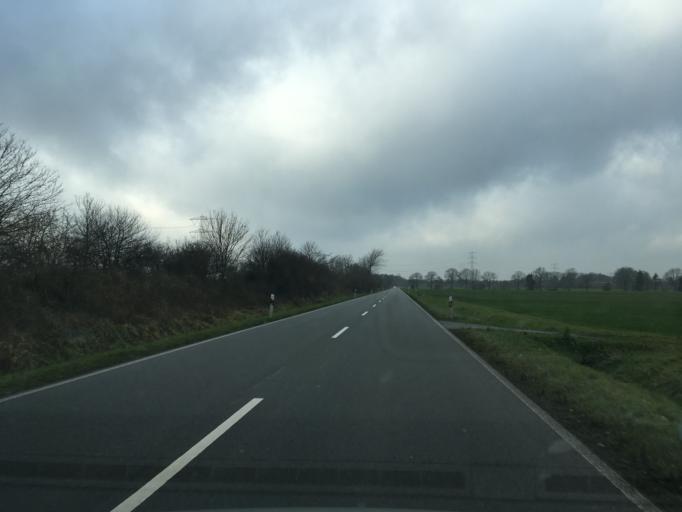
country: DE
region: North Rhine-Westphalia
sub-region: Regierungsbezirk Munster
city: Gronau
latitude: 52.1947
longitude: 6.9900
